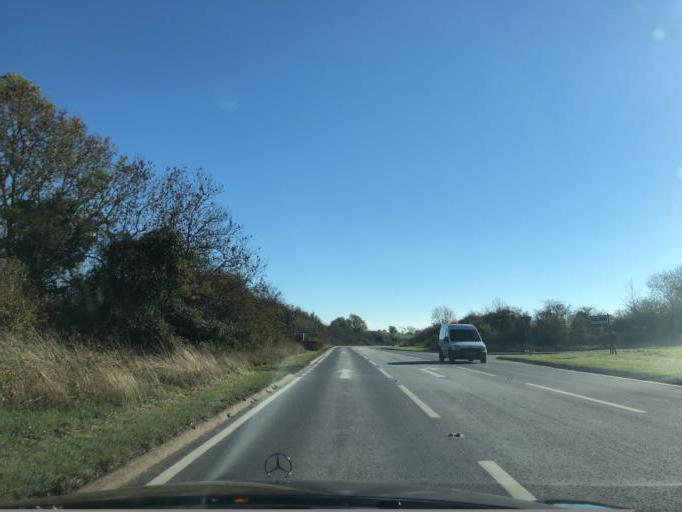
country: GB
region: England
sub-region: Warwickshire
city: Southam
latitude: 52.2317
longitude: -1.3898
